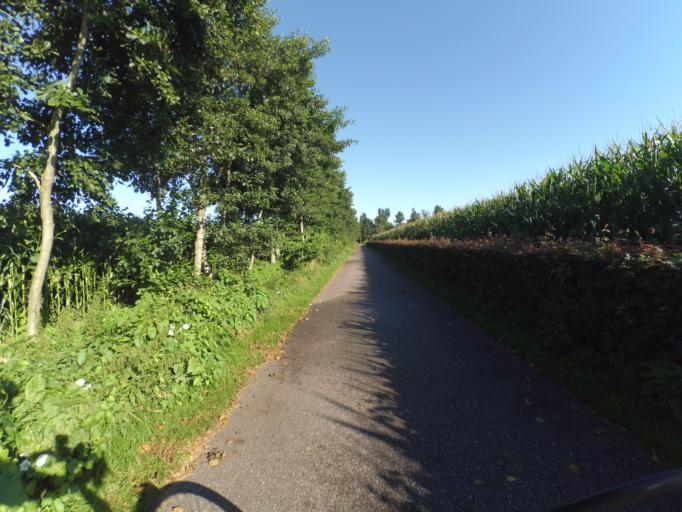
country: NL
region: Friesland
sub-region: Gemeente Achtkarspelen
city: Buitenpost
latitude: 53.2600
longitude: 6.1417
